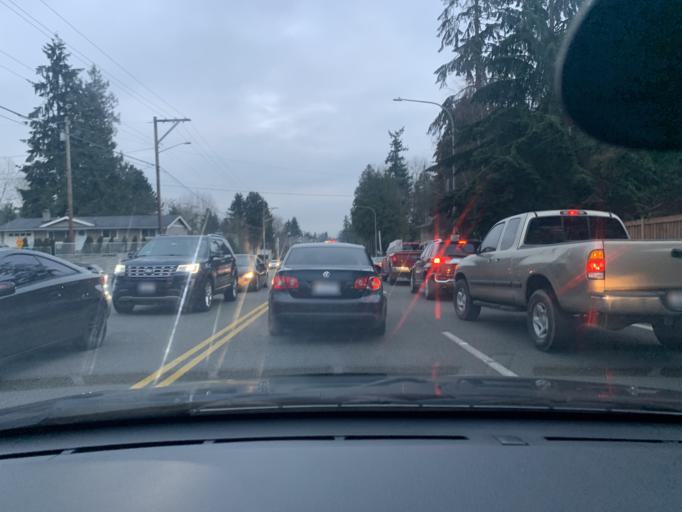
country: US
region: Washington
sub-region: Snohomish County
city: Mill Creek
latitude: 47.8965
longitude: -122.2275
